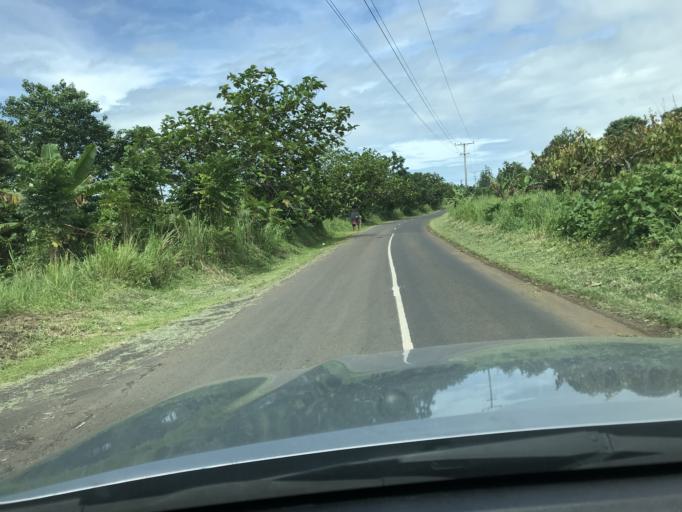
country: WS
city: Fasito`outa
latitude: -13.8593
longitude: -171.9082
